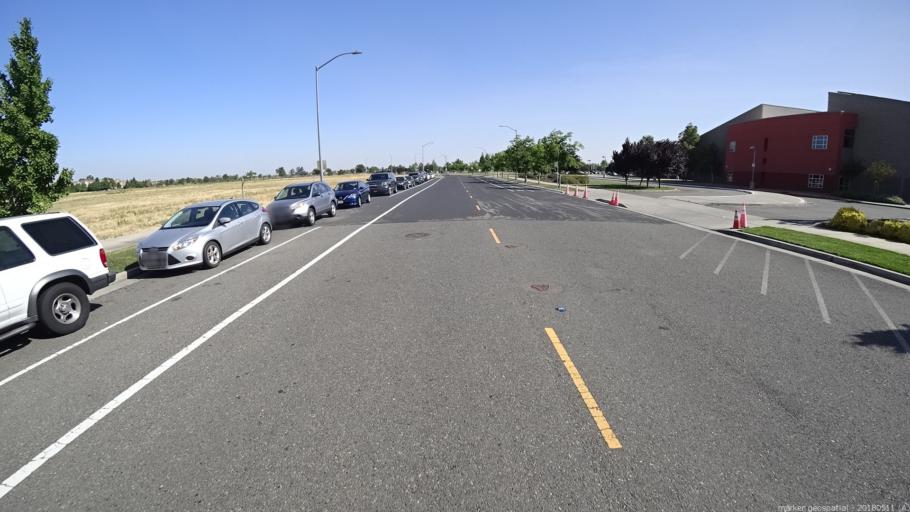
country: US
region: California
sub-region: Sacramento County
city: Rio Linda
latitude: 38.6577
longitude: -121.5186
